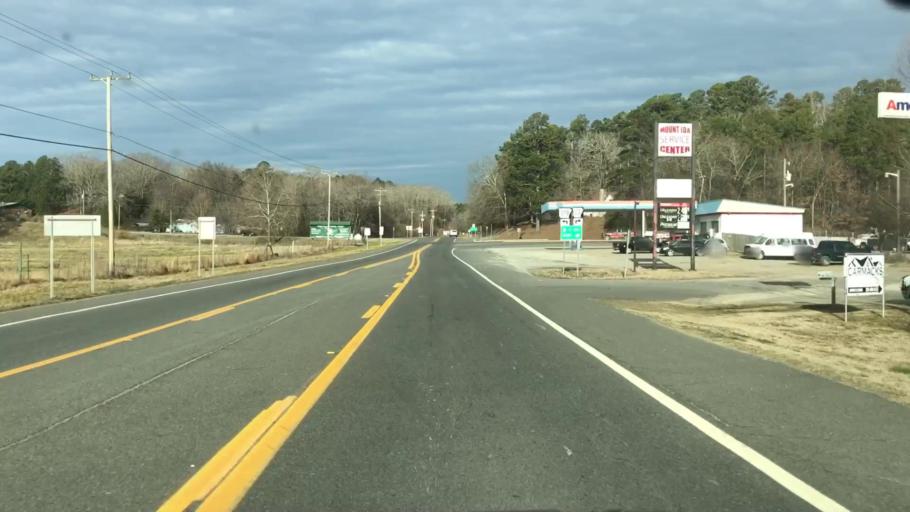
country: US
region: Arkansas
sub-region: Montgomery County
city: Mount Ida
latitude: 34.5616
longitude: -93.6385
